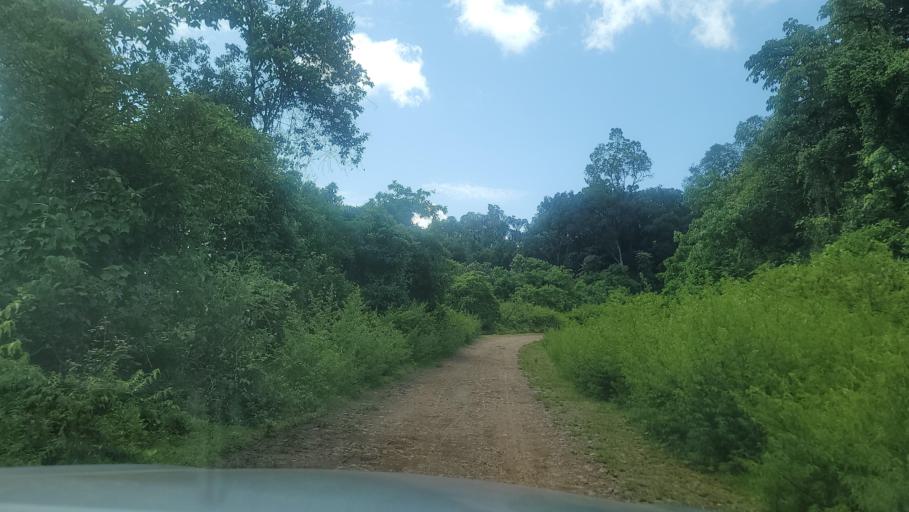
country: ET
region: Southern Nations, Nationalities, and People's Region
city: Bonga
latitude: 7.6704
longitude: 36.2441
